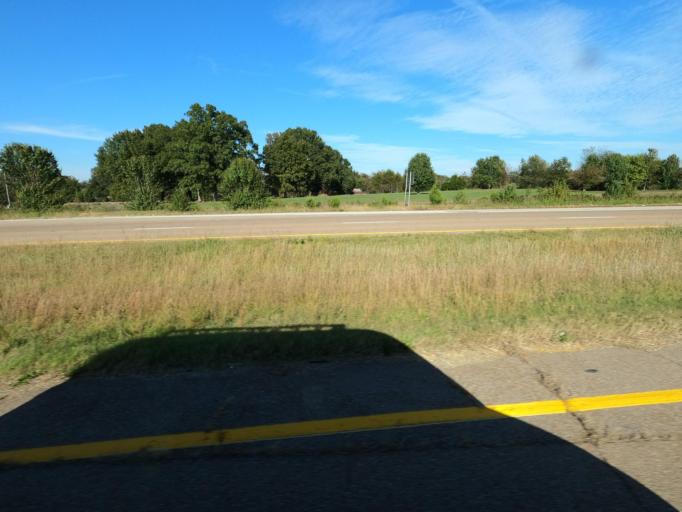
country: US
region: Tennessee
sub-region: Crockett County
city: Alamo
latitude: 35.7741
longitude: -89.1261
